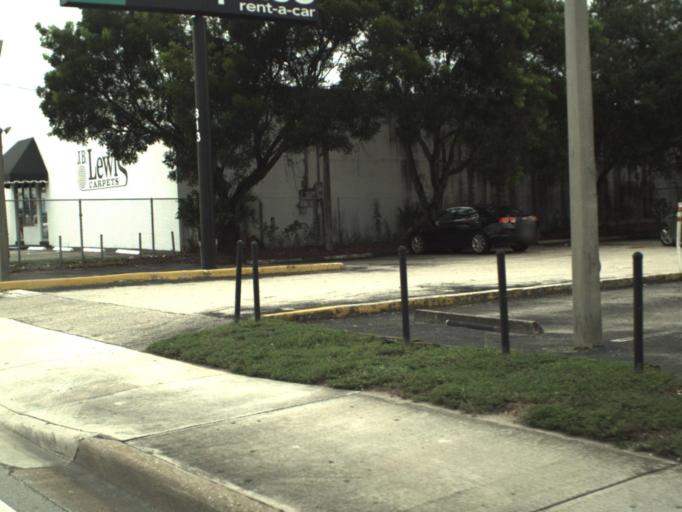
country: US
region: Florida
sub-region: Palm Beach County
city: Haverhill
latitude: 26.6892
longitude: -80.1118
